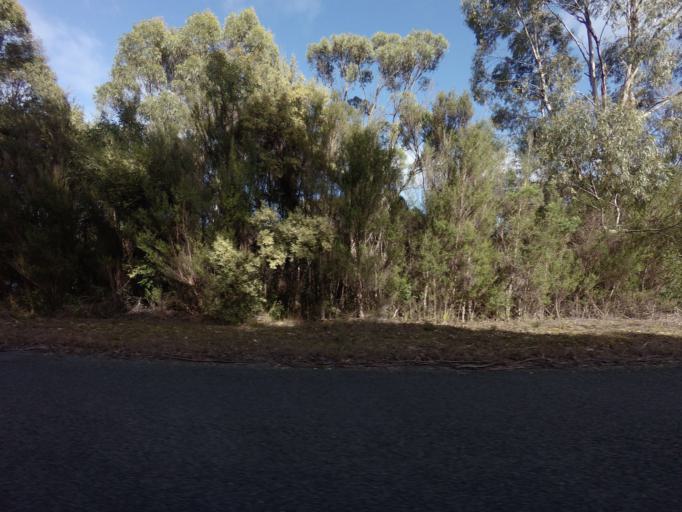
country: AU
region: Tasmania
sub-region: Huon Valley
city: Geeveston
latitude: -42.8249
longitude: 146.1251
